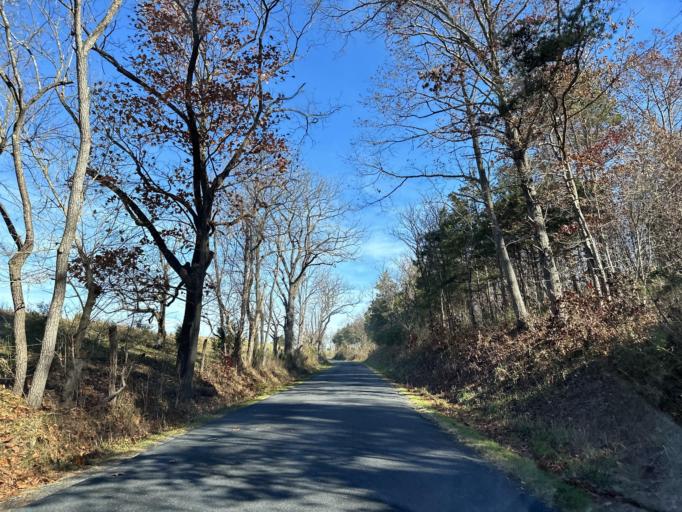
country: US
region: Virginia
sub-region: Augusta County
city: Weyers Cave
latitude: 38.2380
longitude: -78.9215
